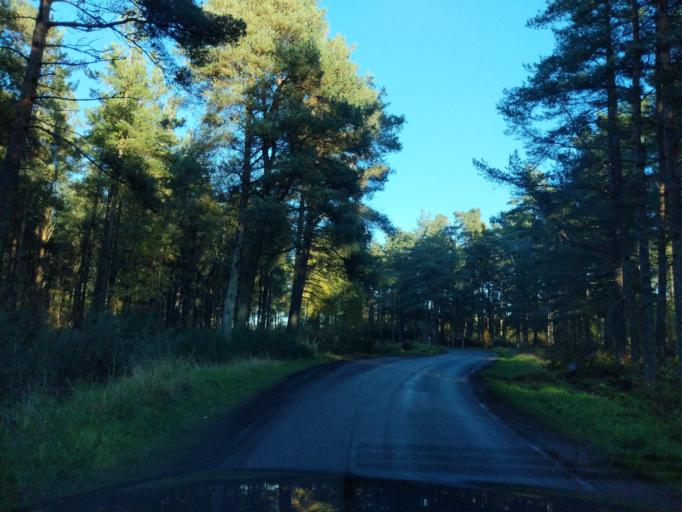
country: GB
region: Scotland
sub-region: Fife
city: Leuchars
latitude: 56.4070
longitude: -2.8187
